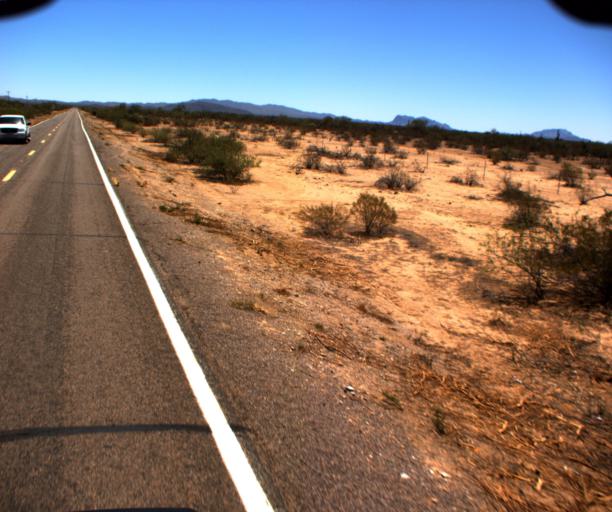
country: US
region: Arizona
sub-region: Pima County
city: Sells
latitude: 32.1824
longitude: -112.3452
